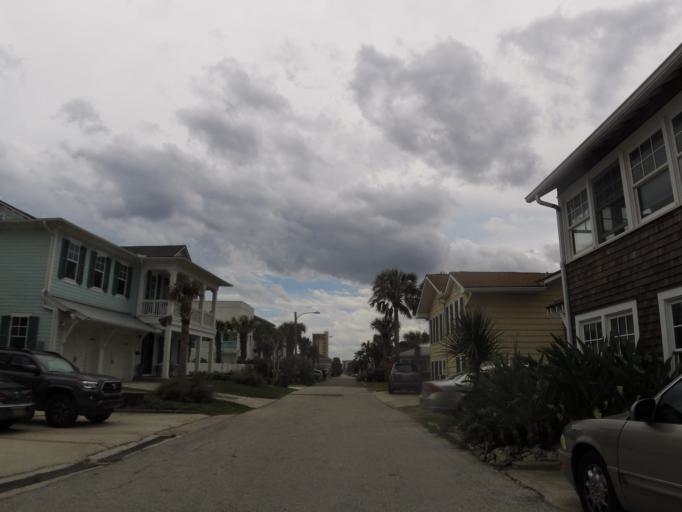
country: US
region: Florida
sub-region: Duval County
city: Neptune Beach
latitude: 30.3126
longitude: -81.3935
